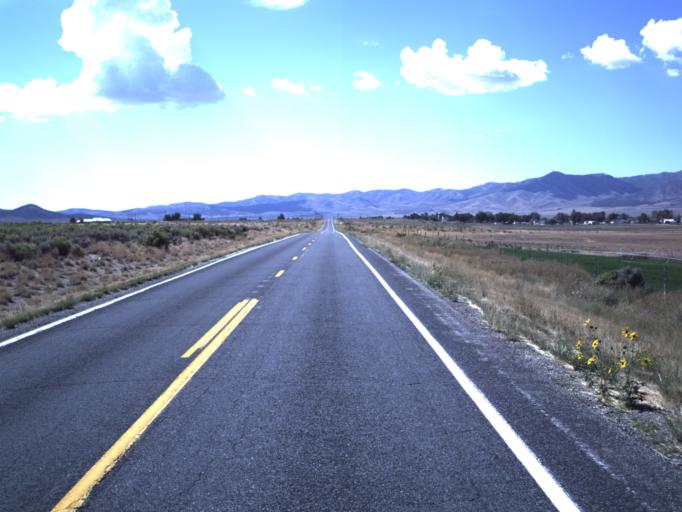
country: US
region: Utah
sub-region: Tooele County
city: Tooele
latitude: 40.1100
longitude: -112.4308
